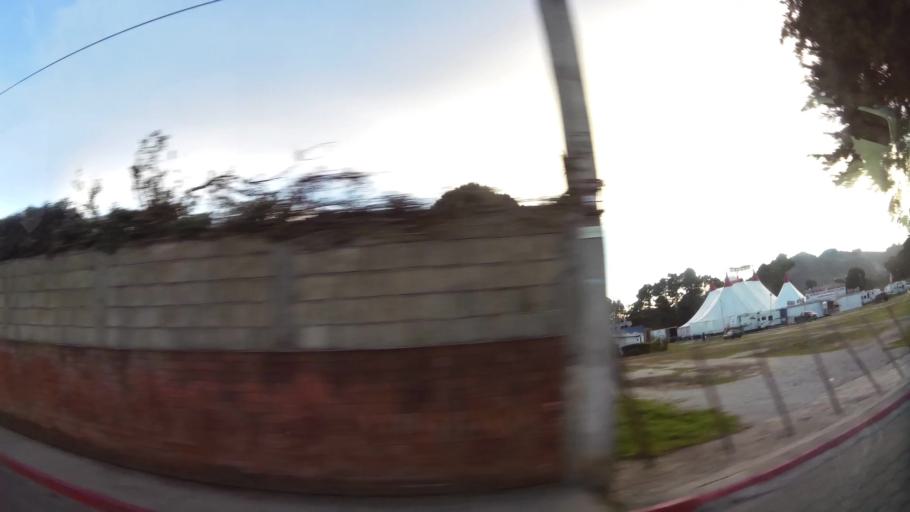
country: GT
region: Sacatepequez
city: San Lucas Sacatepequez
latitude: 14.6105
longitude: -90.6619
